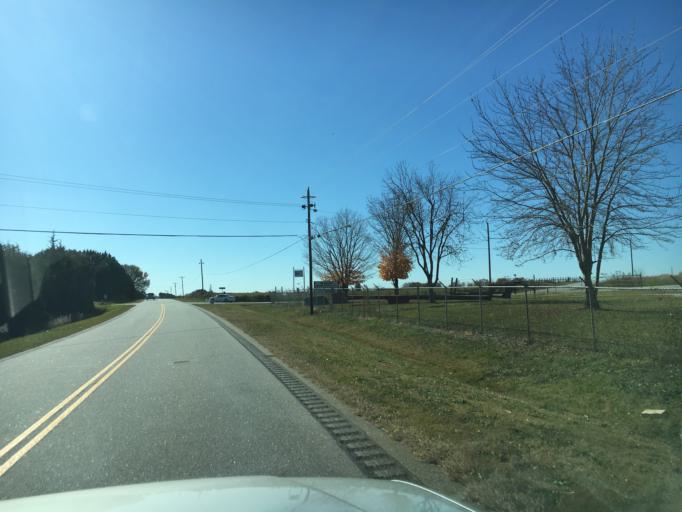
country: US
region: South Carolina
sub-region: Anderson County
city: Centerville
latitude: 34.5001
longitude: -82.7727
